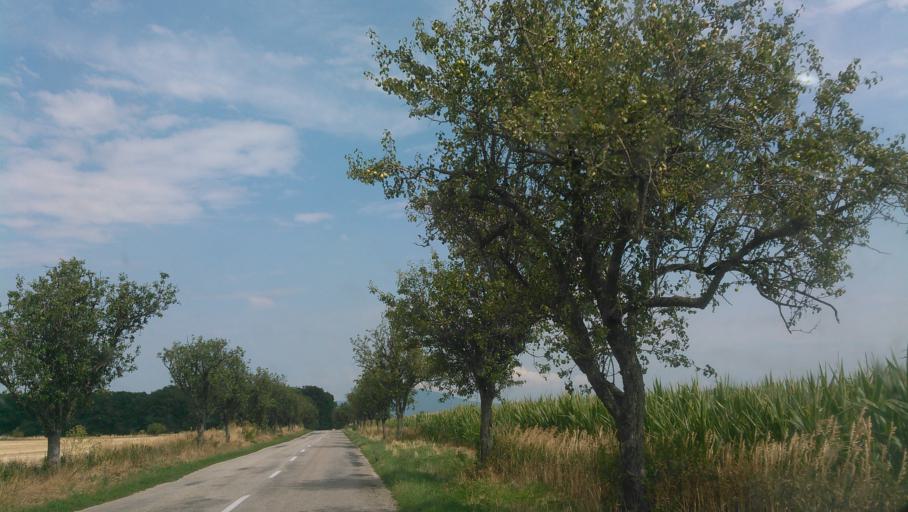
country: SK
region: Nitriansky
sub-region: Okres Nitra
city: Nitra
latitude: 48.5002
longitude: 18.0232
